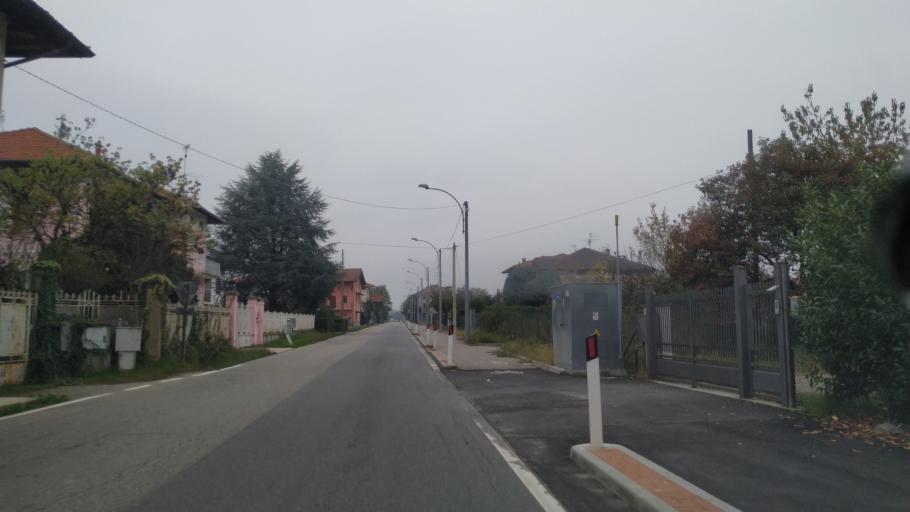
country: IT
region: Piedmont
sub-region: Provincia di Biella
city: Lessona
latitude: 45.5689
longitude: 8.2108
